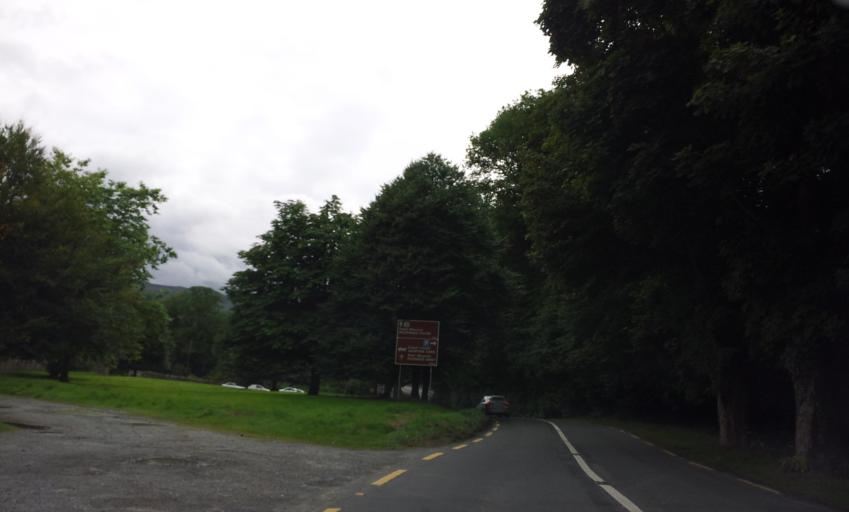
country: IE
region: Munster
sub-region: Ciarrai
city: Cill Airne
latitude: 52.0272
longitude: -9.4882
